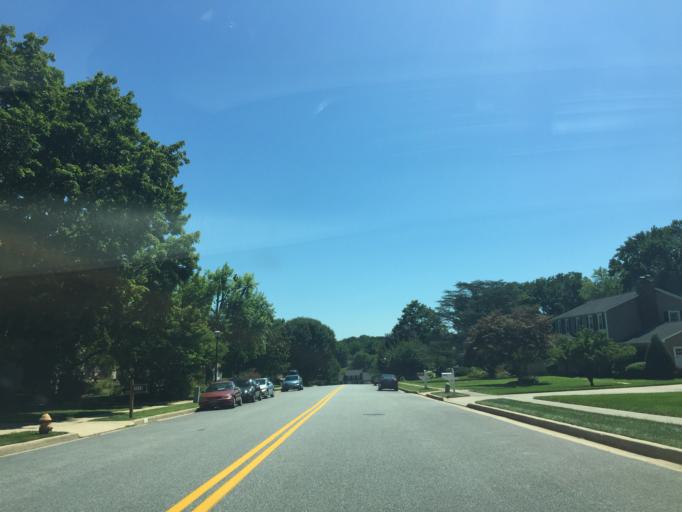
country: US
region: Maryland
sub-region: Baltimore County
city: Timonium
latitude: 39.4726
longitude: -76.6039
